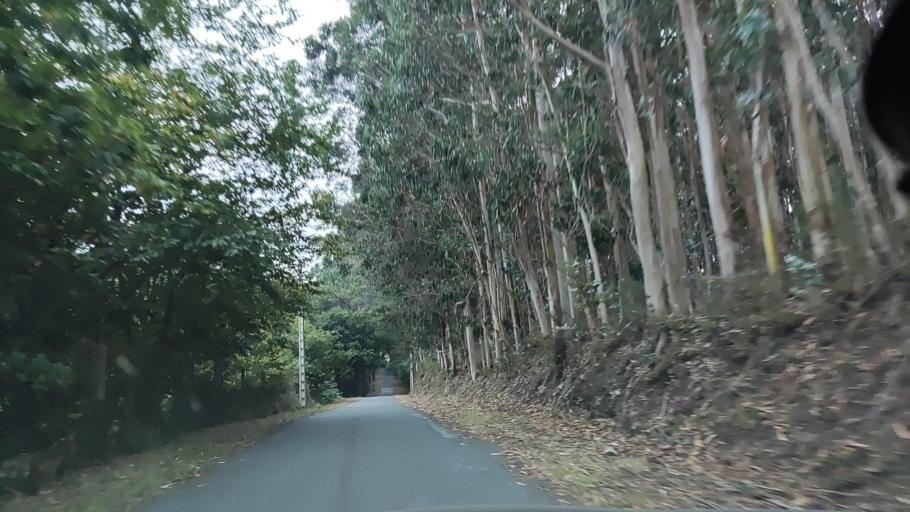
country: ES
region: Galicia
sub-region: Provincia de Pontevedra
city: Catoira
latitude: 42.7034
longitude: -8.7249
